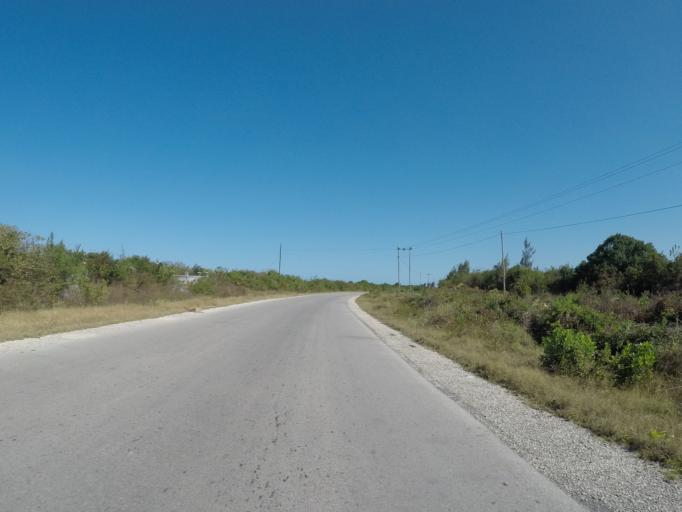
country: TZ
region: Zanzibar Central/South
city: Nganane
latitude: -6.1694
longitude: 39.5258
